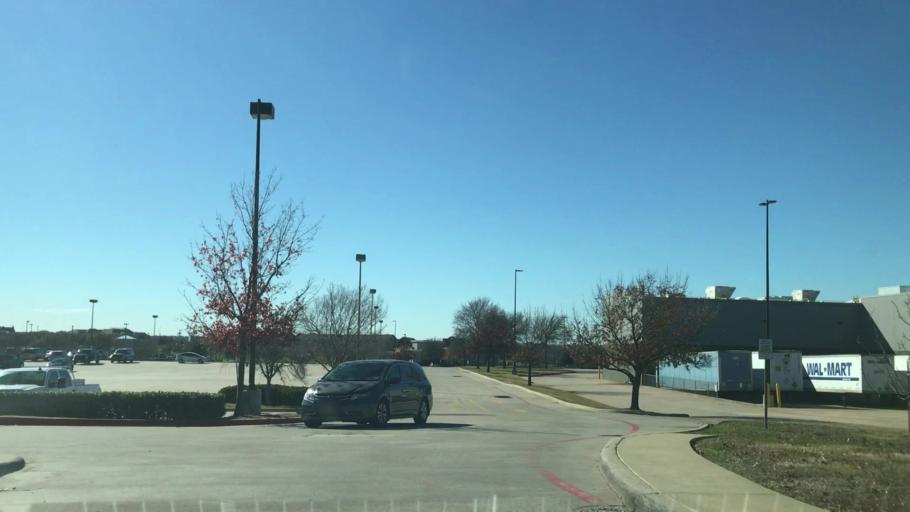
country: US
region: Texas
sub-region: Dallas County
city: Coppell
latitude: 32.9202
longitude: -96.9608
